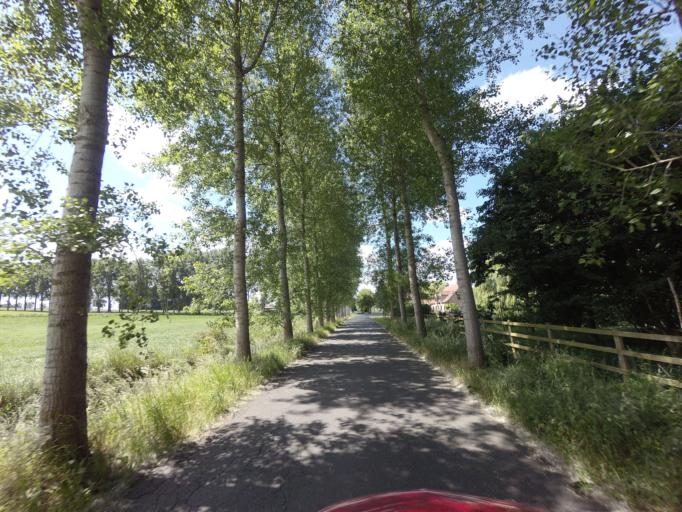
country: BE
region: Flanders
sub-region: Provincie Oost-Vlaanderen
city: Knesselare
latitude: 51.1671
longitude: 3.4017
